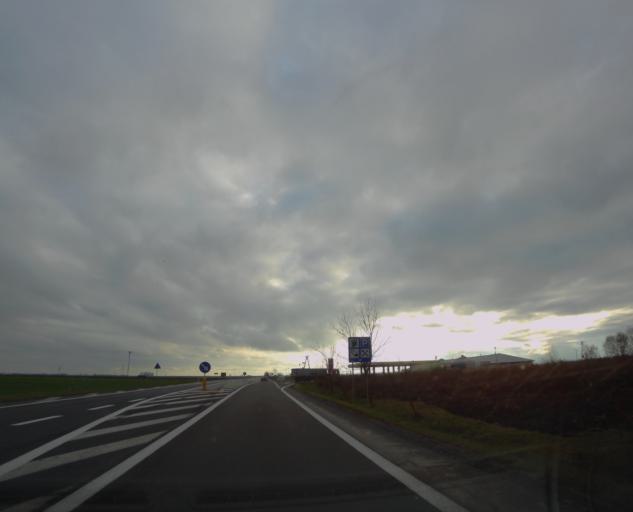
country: PL
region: Subcarpathian Voivodeship
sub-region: Powiat jaroslawski
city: Radymno
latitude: 49.9233
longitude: 22.8208
